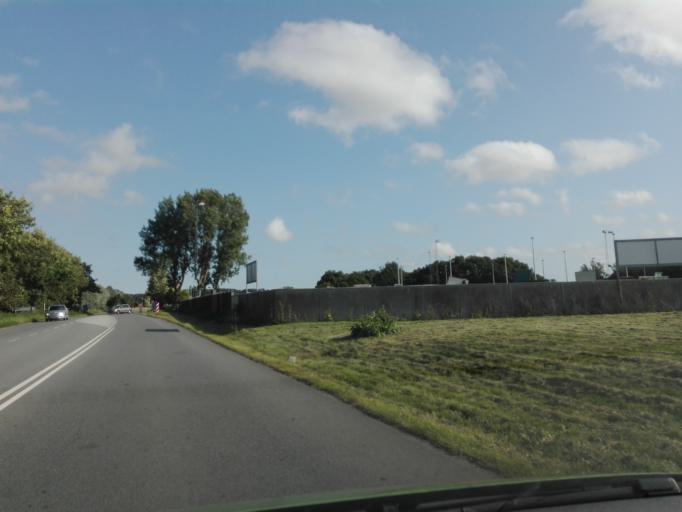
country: DK
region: Central Jutland
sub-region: Arhus Kommune
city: Lystrup
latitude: 56.2154
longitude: 10.2342
